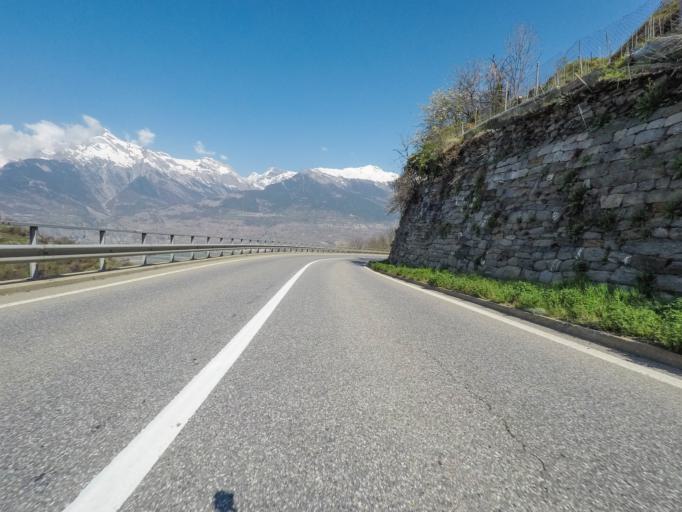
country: CH
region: Valais
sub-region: Conthey District
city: Basse-Nendaz
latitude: 46.1964
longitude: 7.3224
